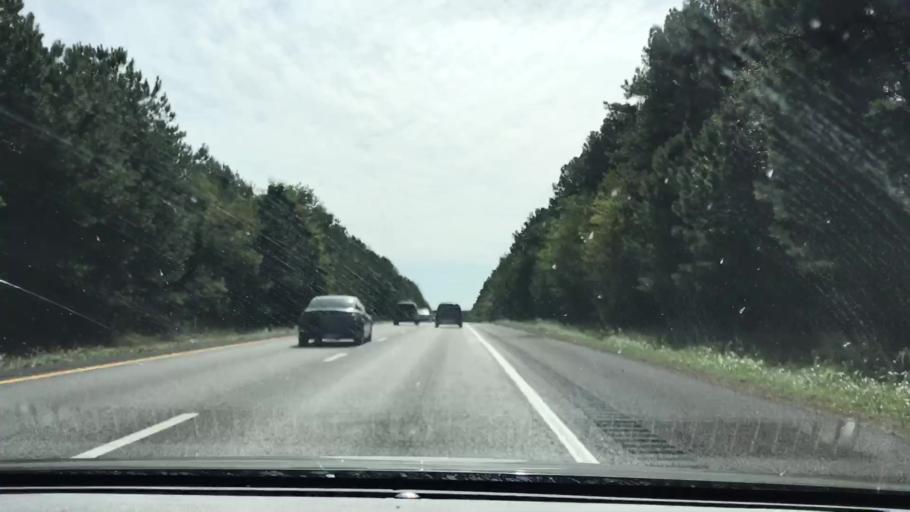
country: US
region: Tennessee
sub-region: Robertson County
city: Cross Plains
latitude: 36.5553
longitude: -86.6290
